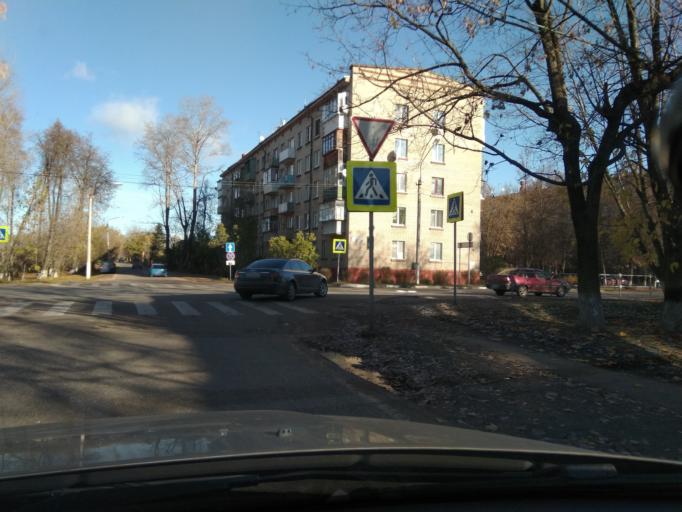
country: RU
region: Moskovskaya
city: Istra
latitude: 55.9197
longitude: 36.8633
